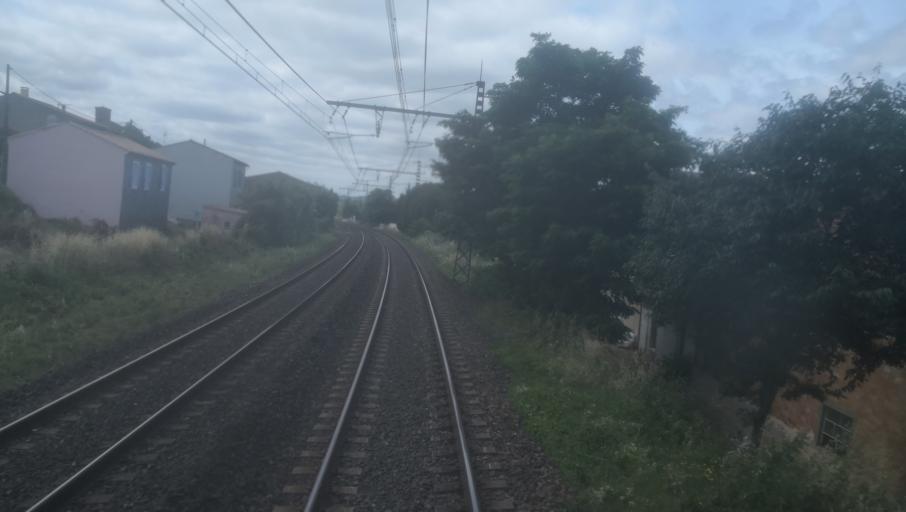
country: FR
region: Languedoc-Roussillon
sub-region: Departement de l'Aude
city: Capendu
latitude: 43.1854
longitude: 2.5142
